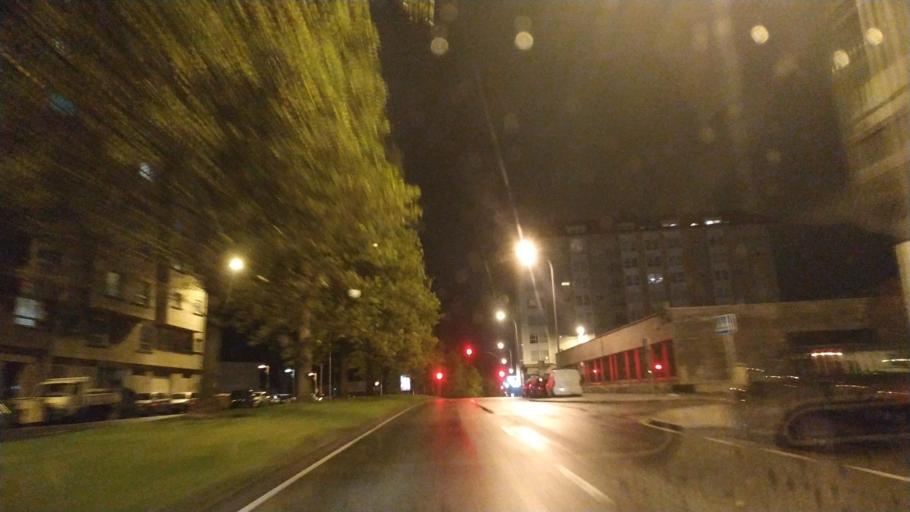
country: ES
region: Galicia
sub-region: Provincia da Coruna
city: A Coruna
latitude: 43.3532
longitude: -8.4152
